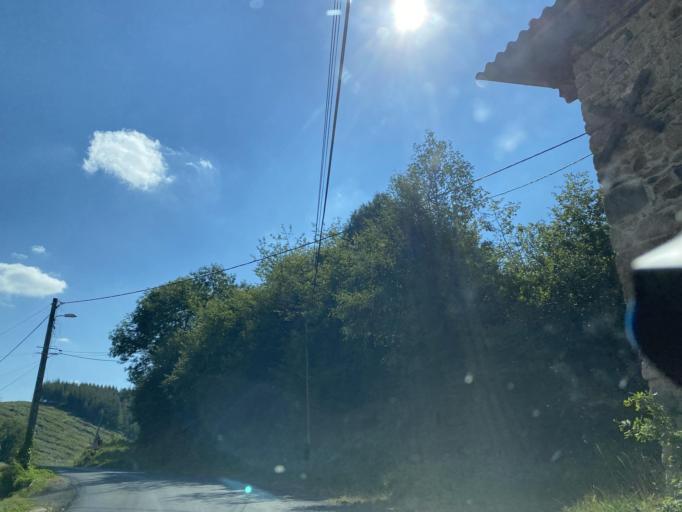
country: FR
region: Auvergne
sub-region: Departement du Puy-de-Dome
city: Celles-sur-Durolle
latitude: 45.8510
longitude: 3.6409
